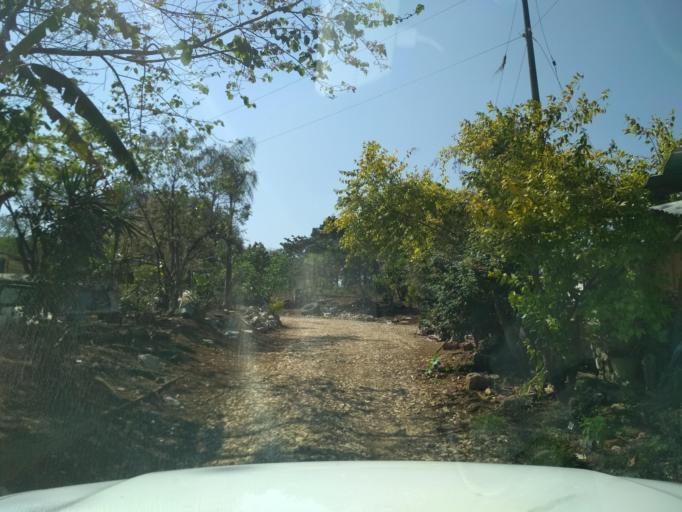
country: MX
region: Veracruz
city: Amatlan de los Reyes
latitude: 18.8482
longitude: -96.9039
